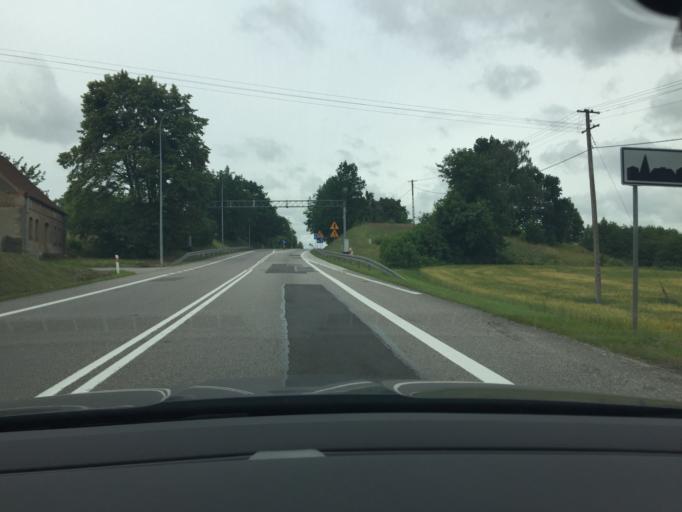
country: PL
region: Pomeranian Voivodeship
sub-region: Powiat starogardzki
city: Smetowo Graniczne
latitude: 53.7508
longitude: 18.7573
